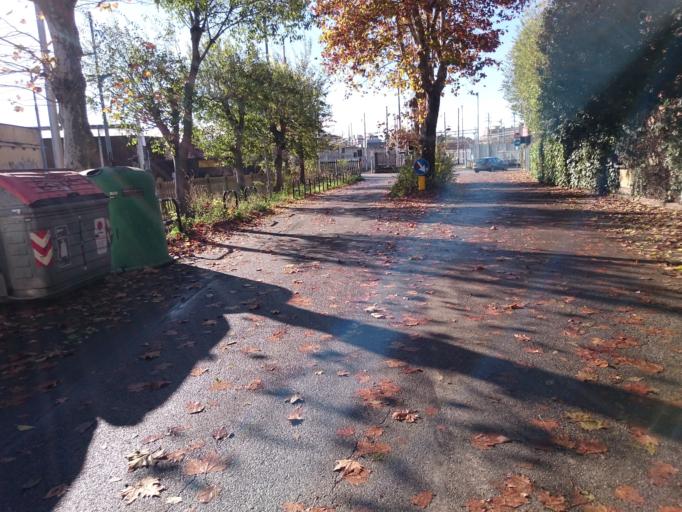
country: IT
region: Emilia-Romagna
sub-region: Provincia di Bologna
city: Bologna
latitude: 44.5087
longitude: 11.3362
